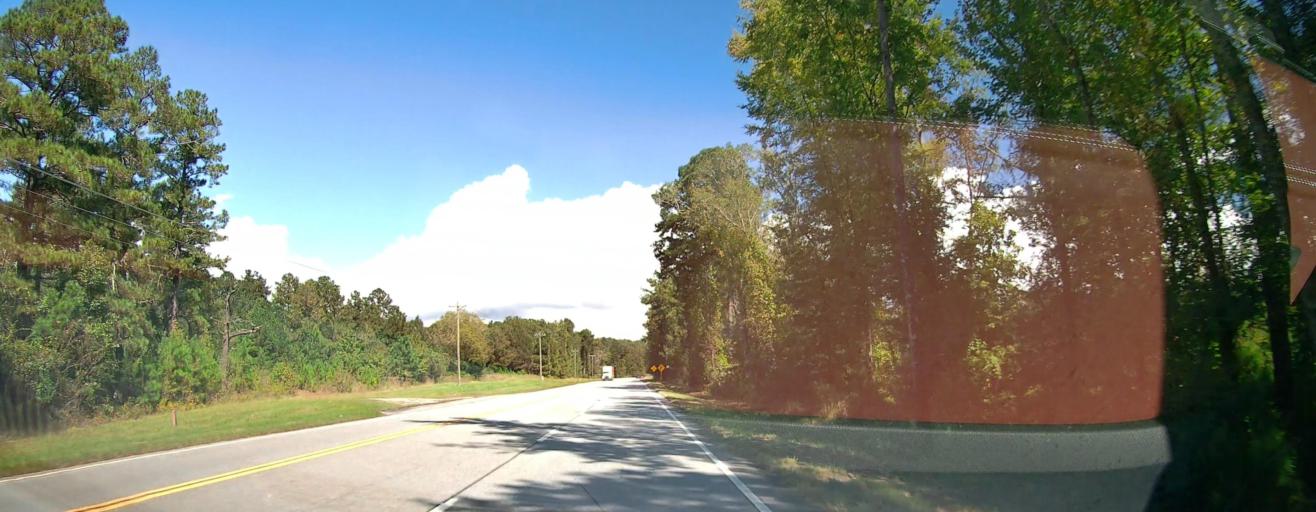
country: US
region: Georgia
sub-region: Jones County
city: Gray
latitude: 32.9362
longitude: -83.4972
